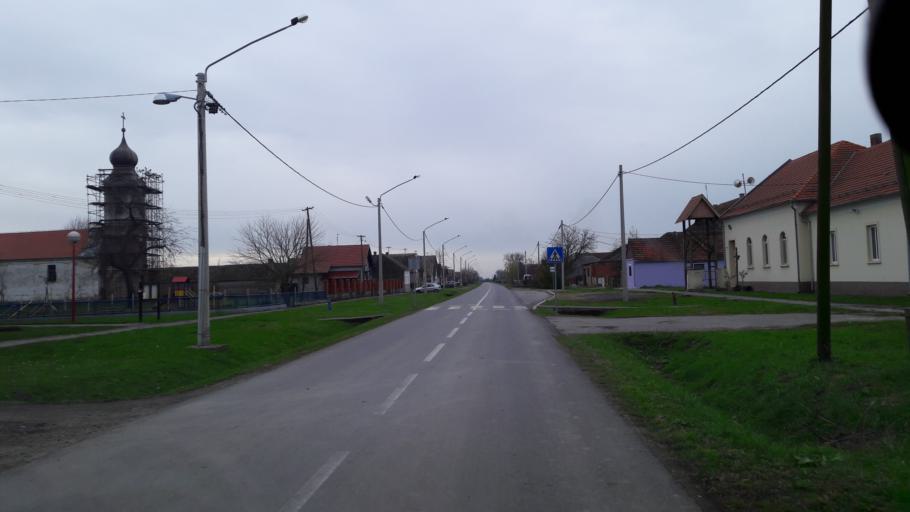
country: HR
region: Osjecko-Baranjska
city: Vladislavci
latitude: 45.4515
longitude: 18.5587
